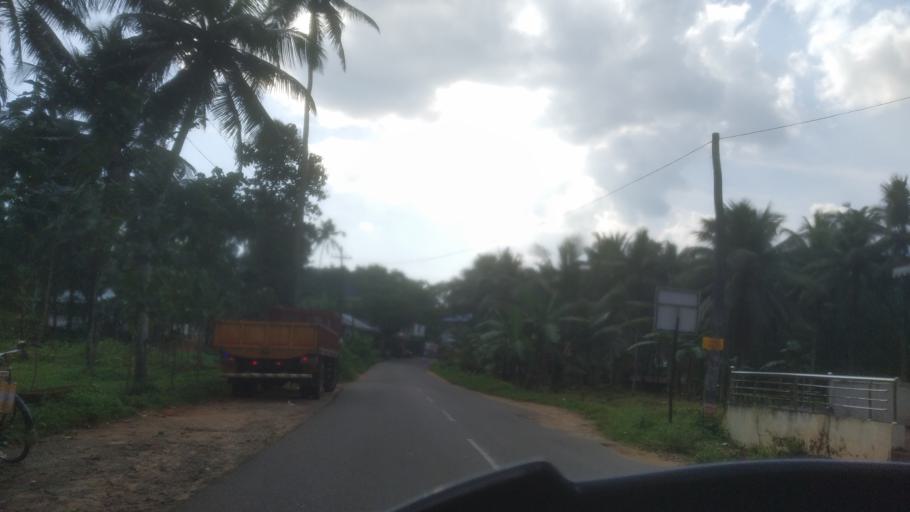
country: IN
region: Kerala
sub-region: Ernakulam
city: Kotamangalam
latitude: 10.0037
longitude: 76.6631
